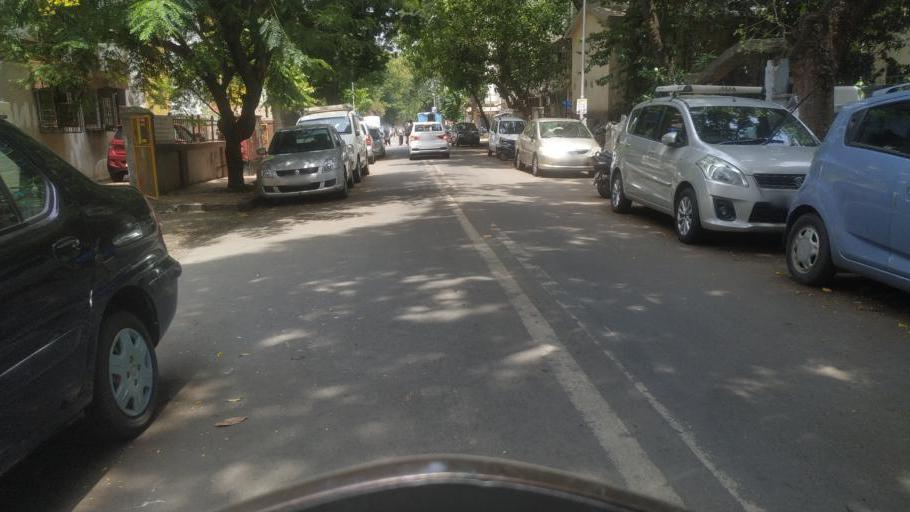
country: IN
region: Maharashtra
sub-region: Mumbai Suburban
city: Mumbai
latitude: 19.0177
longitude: 72.8361
